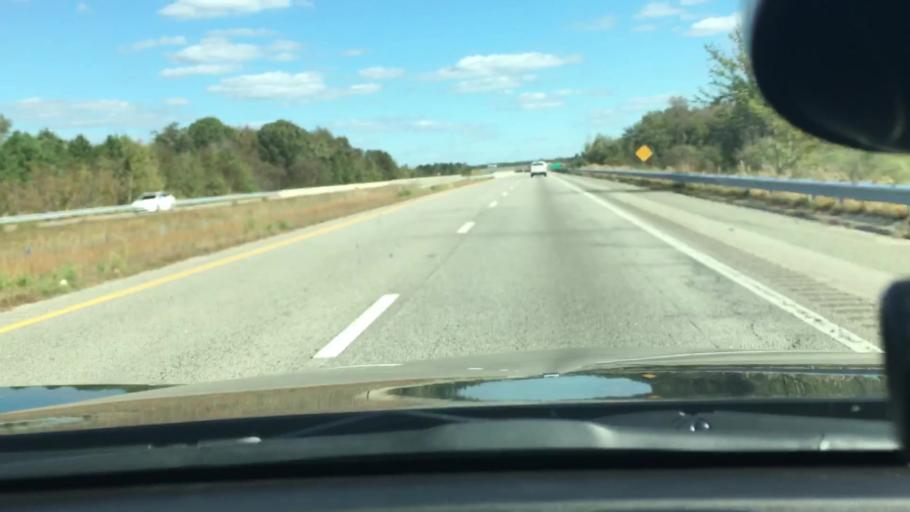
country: US
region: North Carolina
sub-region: Wilson County
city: Wilson
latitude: 35.6742
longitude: -77.9147
